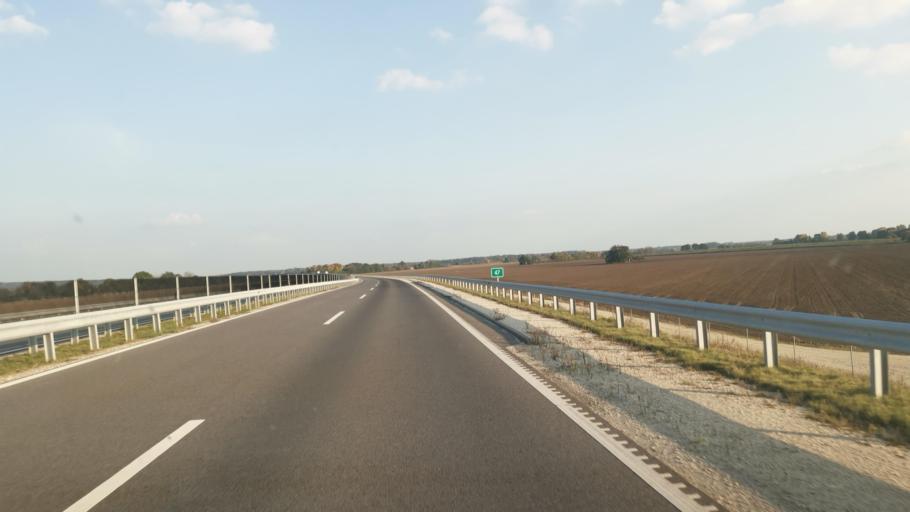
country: HU
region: Gyor-Moson-Sopron
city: Kapuvar
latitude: 47.5741
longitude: 17.0012
